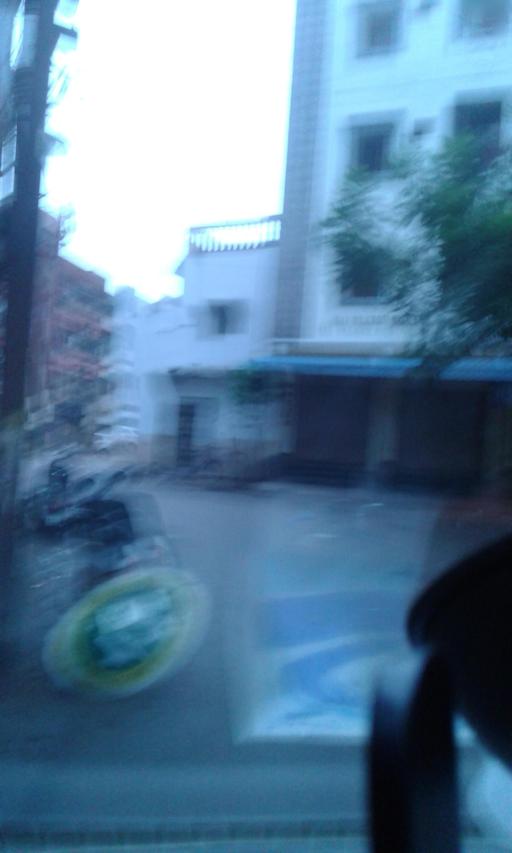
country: IN
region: Telangana
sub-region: Hyderabad
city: Hyderabad
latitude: 17.3757
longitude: 78.4883
